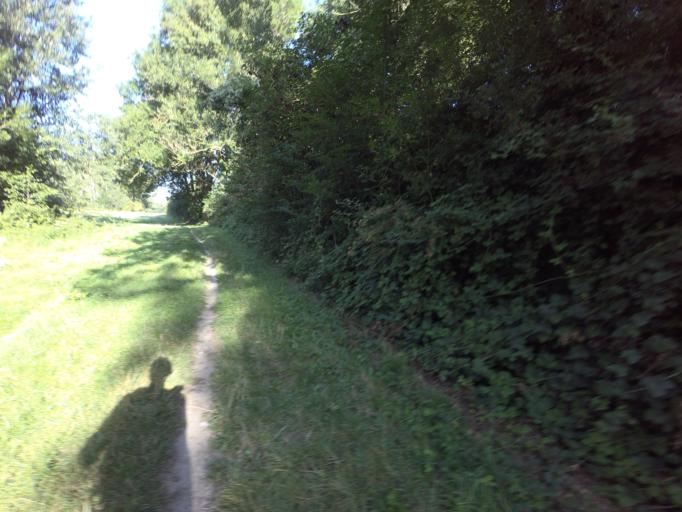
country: NL
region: Limburg
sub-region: Gemeente Simpelveld
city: Simpelveld
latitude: 50.7950
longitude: 5.9847
